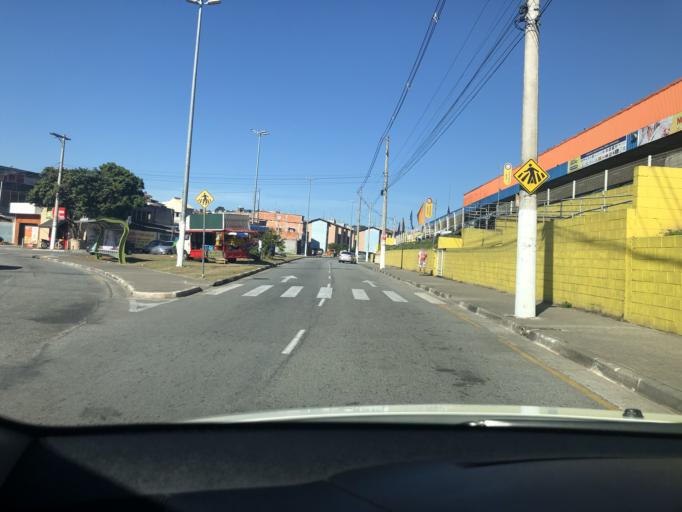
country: BR
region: Sao Paulo
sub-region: Jandira
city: Jandira
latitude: -23.5321
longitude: -46.8922
